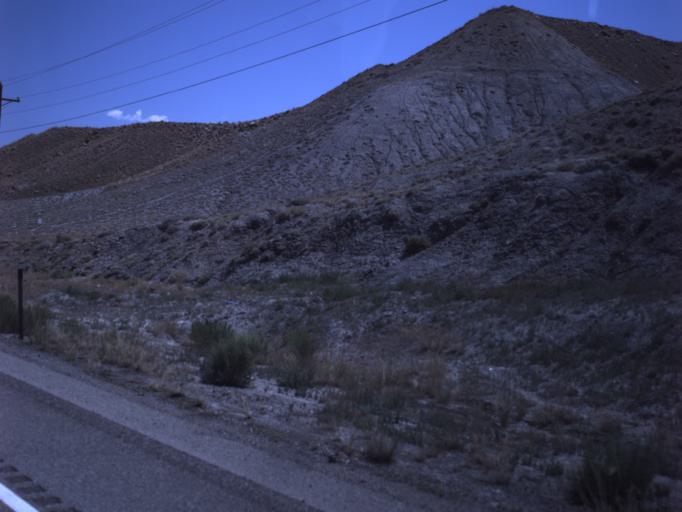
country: US
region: Utah
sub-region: Emery County
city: Ferron
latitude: 39.1508
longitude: -111.0882
